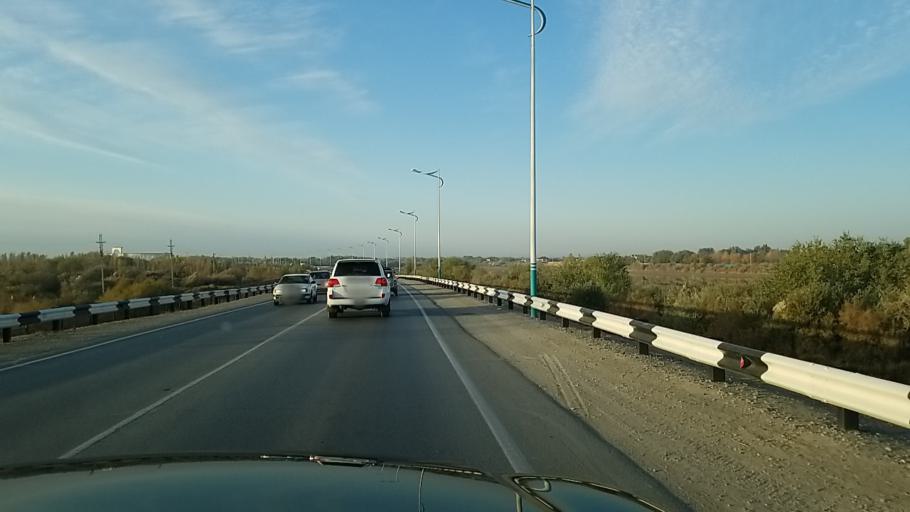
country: KZ
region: Qyzylorda
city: Tasboget
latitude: 44.7803
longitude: 65.5062
